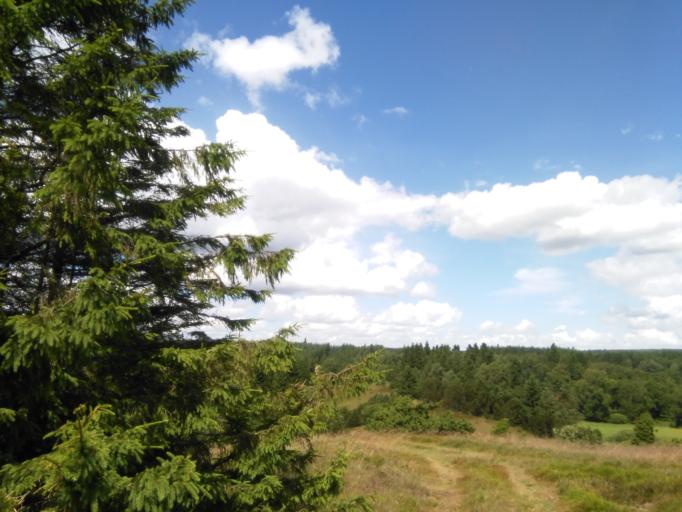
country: DK
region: Central Jutland
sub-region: Silkeborg Kommune
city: Virklund
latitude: 56.0628
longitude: 9.4472
